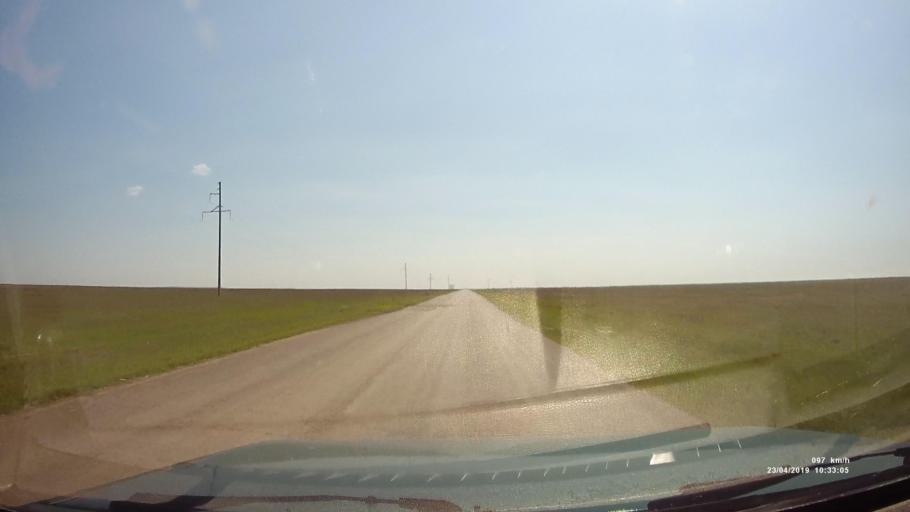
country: RU
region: Kalmykiya
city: Yashalta
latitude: 46.5759
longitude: 42.5900
